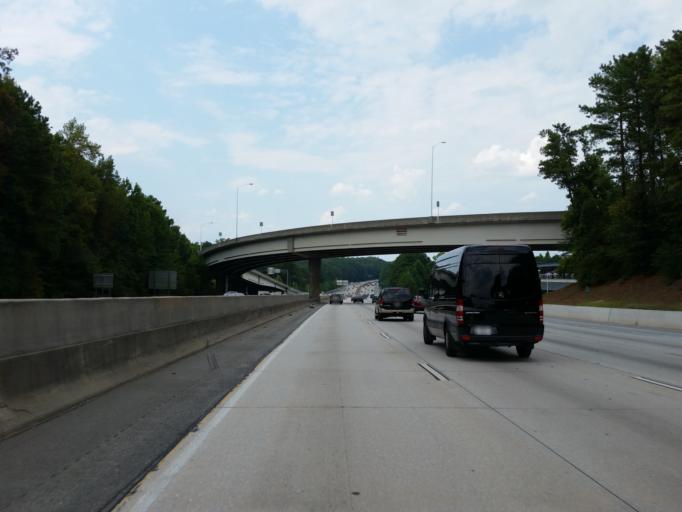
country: US
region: Georgia
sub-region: DeKalb County
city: Dunwoody
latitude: 33.9429
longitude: -84.3580
